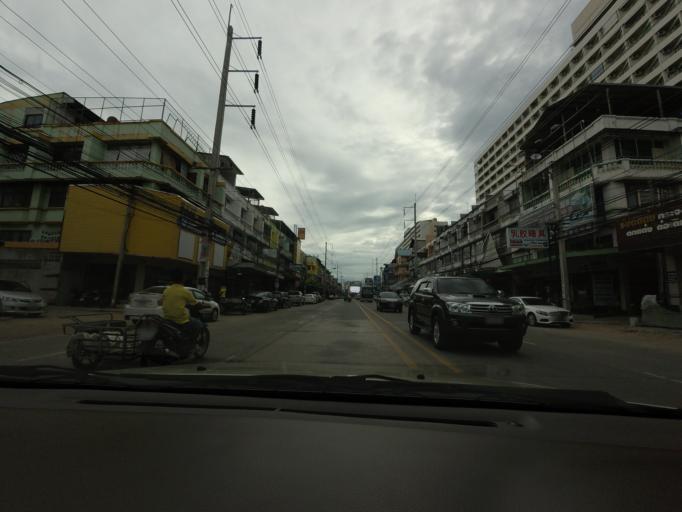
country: TH
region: Chon Buri
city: Phatthaya
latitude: 12.9052
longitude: 100.8728
